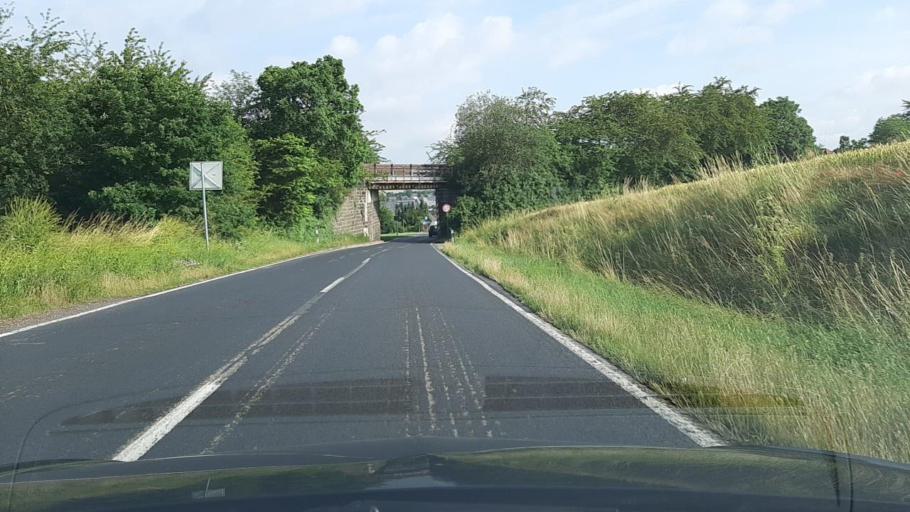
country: DE
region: Rheinland-Pfalz
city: Ochtendung
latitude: 50.3427
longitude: 7.3927
